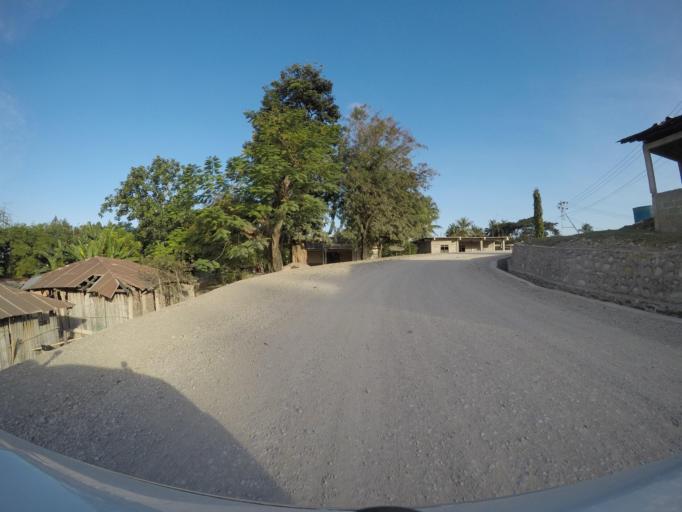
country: TL
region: Viqueque
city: Viqueque
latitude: -8.8212
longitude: 126.5331
